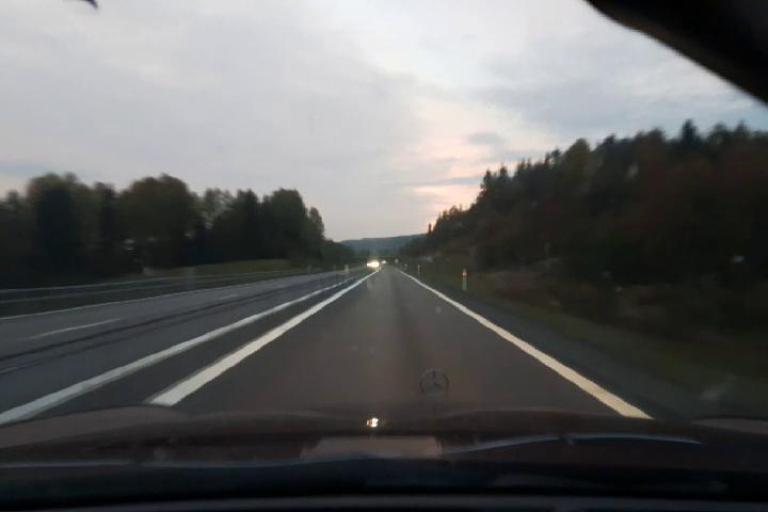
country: SE
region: Vaesternorrland
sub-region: Kramfors Kommun
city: Nordingra
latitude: 62.9343
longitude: 18.0947
